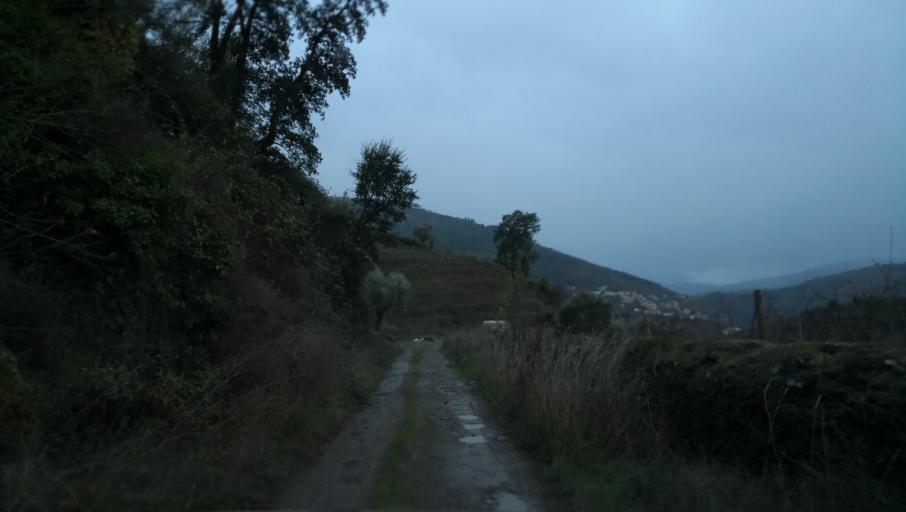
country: PT
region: Vila Real
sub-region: Santa Marta de Penaguiao
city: Santa Marta de Penaguiao
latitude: 41.2343
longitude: -7.7387
